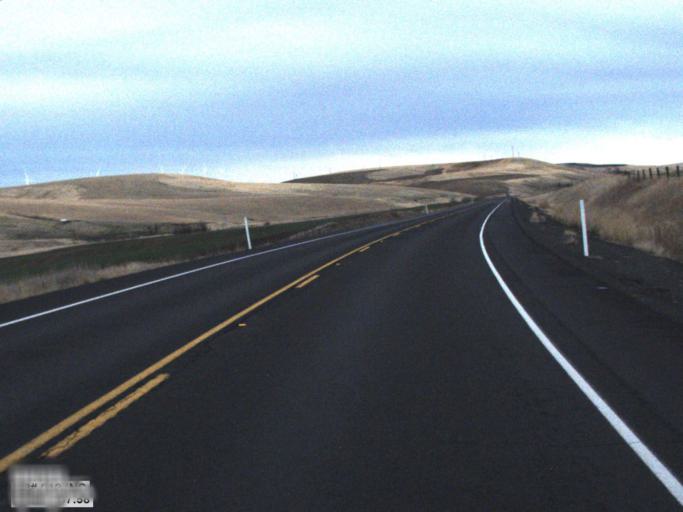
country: US
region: Washington
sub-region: Columbia County
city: Dayton
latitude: 46.5469
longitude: -117.8807
